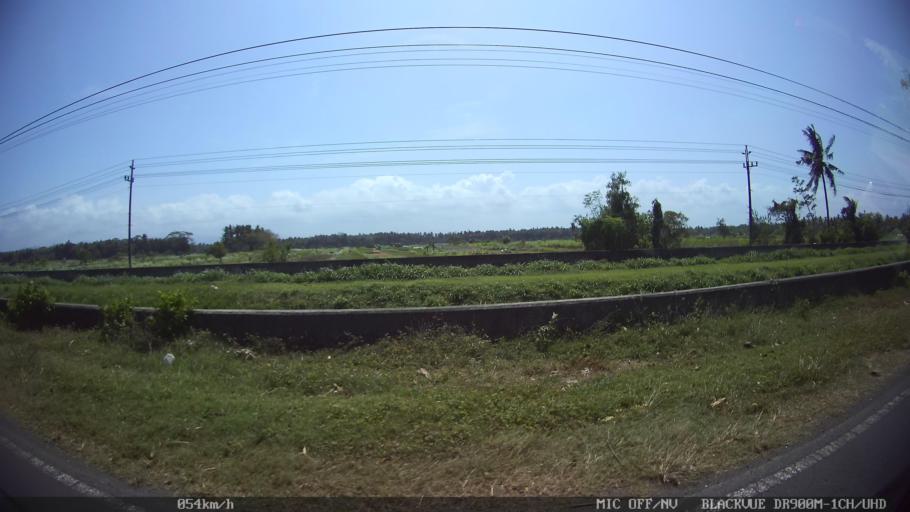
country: ID
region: Daerah Istimewa Yogyakarta
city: Srandakan
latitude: -7.9318
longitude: 110.1403
